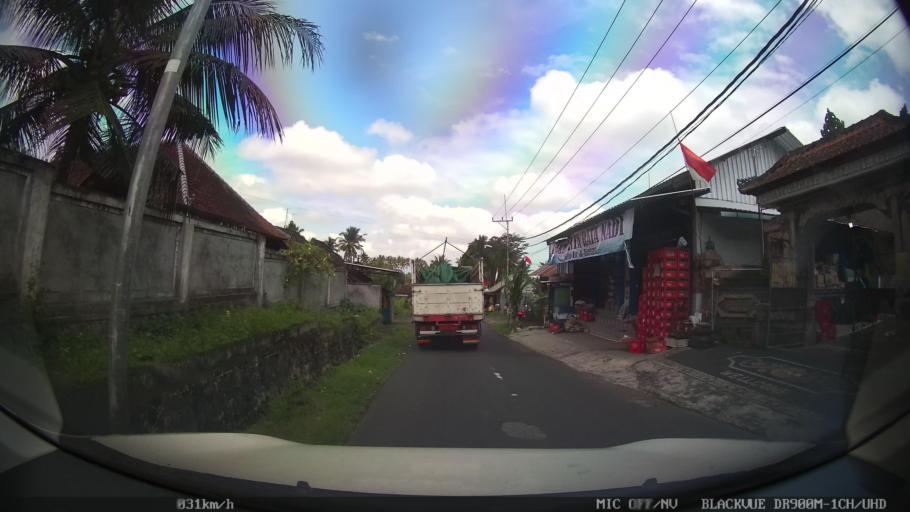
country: ID
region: Bali
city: Banjar Kelodan
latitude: -8.4924
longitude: 115.3688
